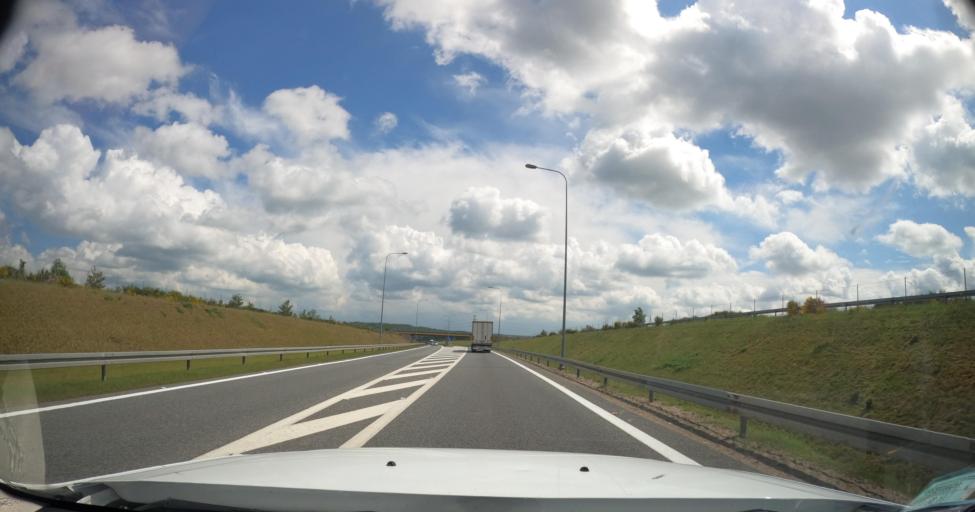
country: PL
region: Pomeranian Voivodeship
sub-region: Powiat slupski
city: Kobylnica
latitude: 54.4257
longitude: 16.9925
